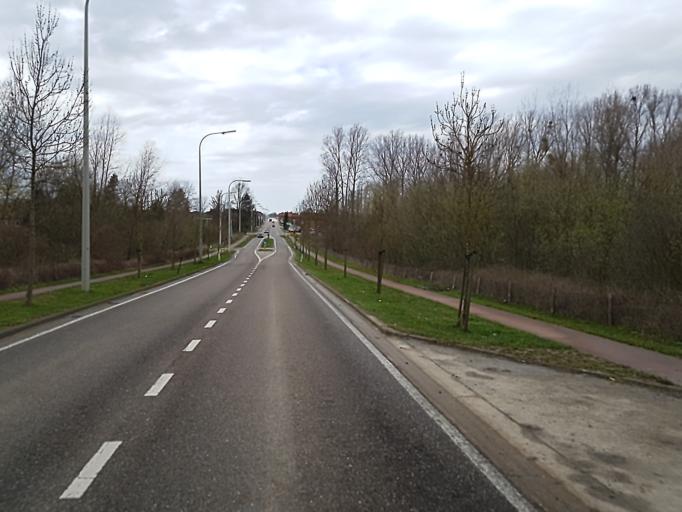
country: BE
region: Flanders
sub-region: Provincie Limburg
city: Tongeren
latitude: 50.7850
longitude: 5.4052
